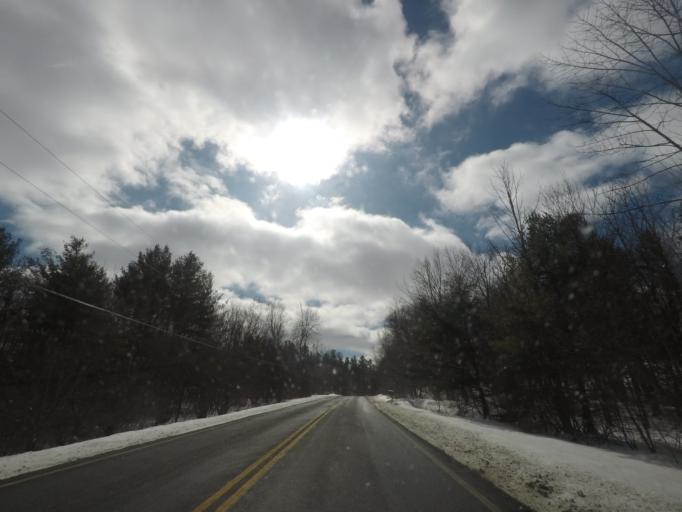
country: US
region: New York
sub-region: Columbia County
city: Chatham
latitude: 42.4115
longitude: -73.5508
